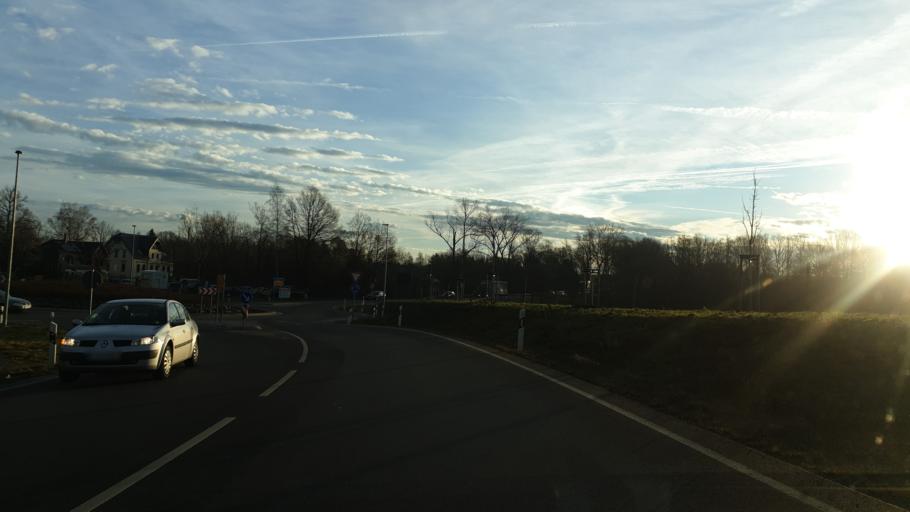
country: DE
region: Saxony
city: Neukirchen
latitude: 50.8086
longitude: 12.8194
